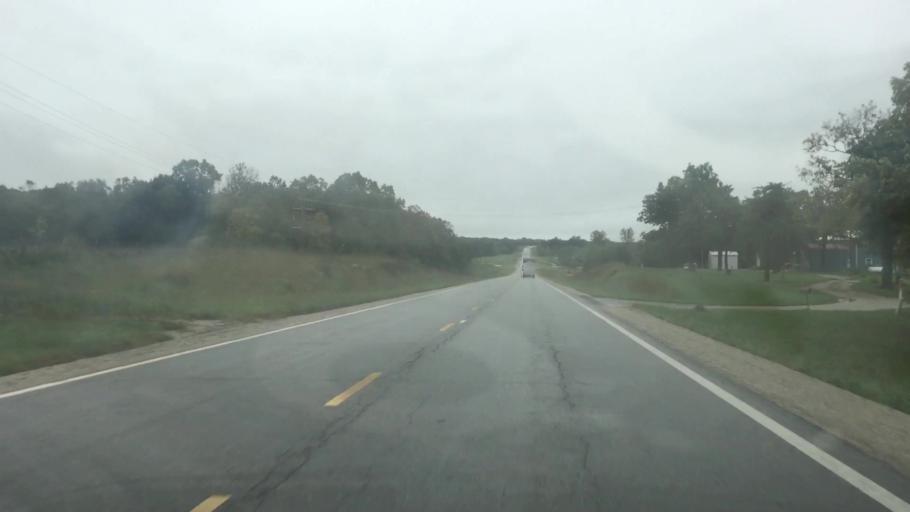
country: US
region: Kansas
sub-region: Anderson County
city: Garnett
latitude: 38.2175
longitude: -95.2487
